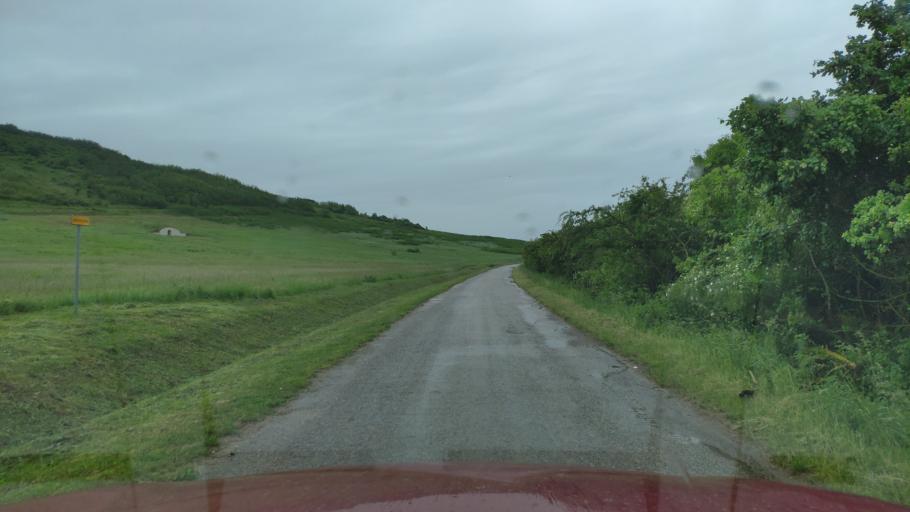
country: HU
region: Borsod-Abauj-Zemplen
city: Satoraljaujhely
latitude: 48.4306
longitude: 21.6961
